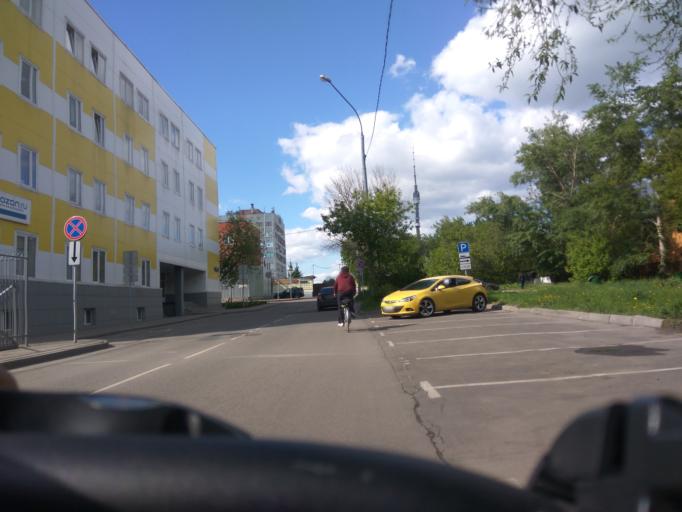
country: RU
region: Moscow
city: Mar'ina Roshcha
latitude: 55.8035
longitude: 37.6078
